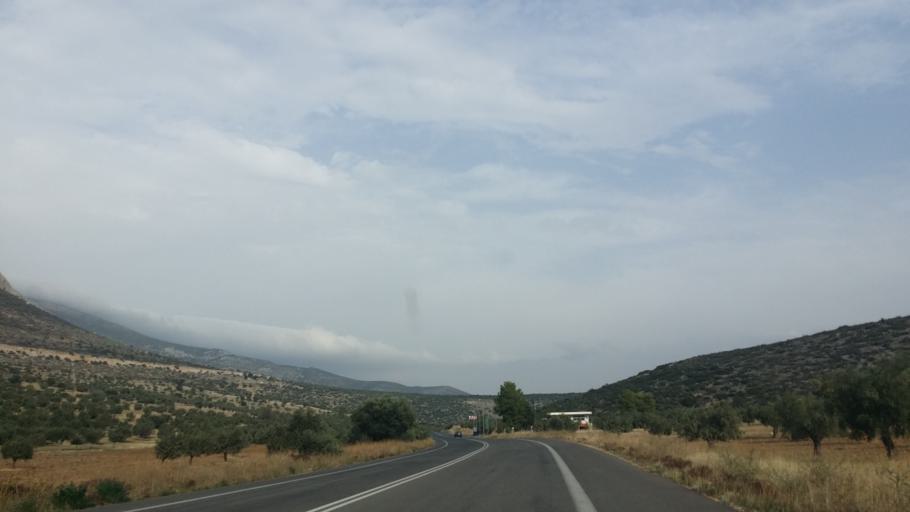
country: GR
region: Central Greece
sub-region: Nomos Voiotias
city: Korini
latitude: 38.2607
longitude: 23.0092
